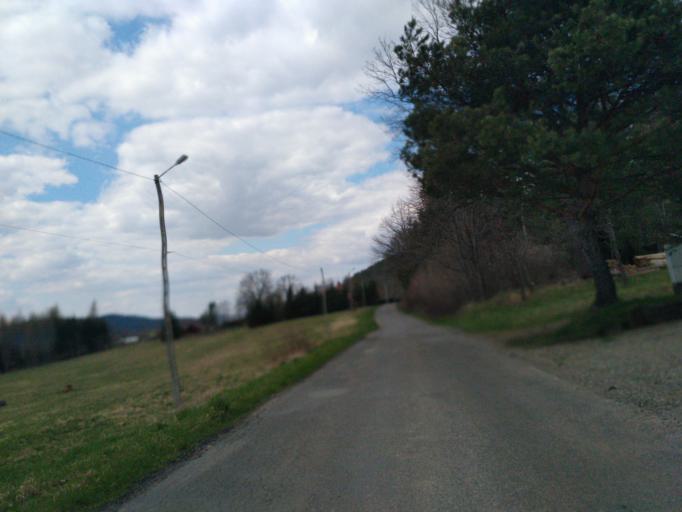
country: PL
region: Subcarpathian Voivodeship
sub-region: Powiat brzozowski
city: Dydnia
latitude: 49.6690
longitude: 22.2863
